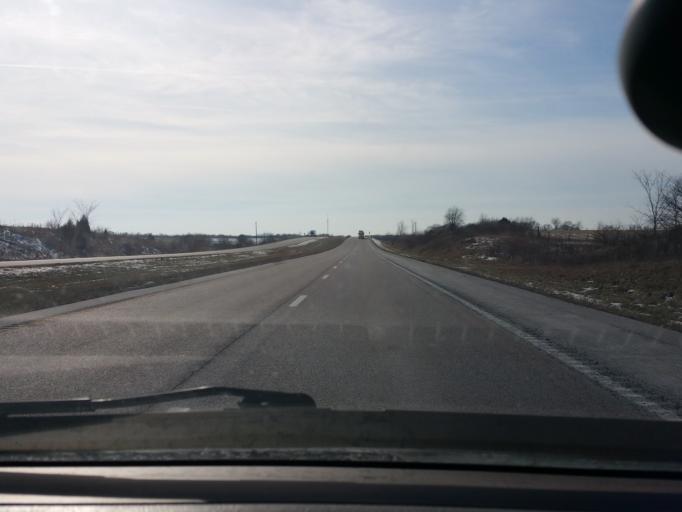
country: US
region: Missouri
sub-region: Clinton County
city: Lathrop
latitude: 39.5174
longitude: -94.2847
